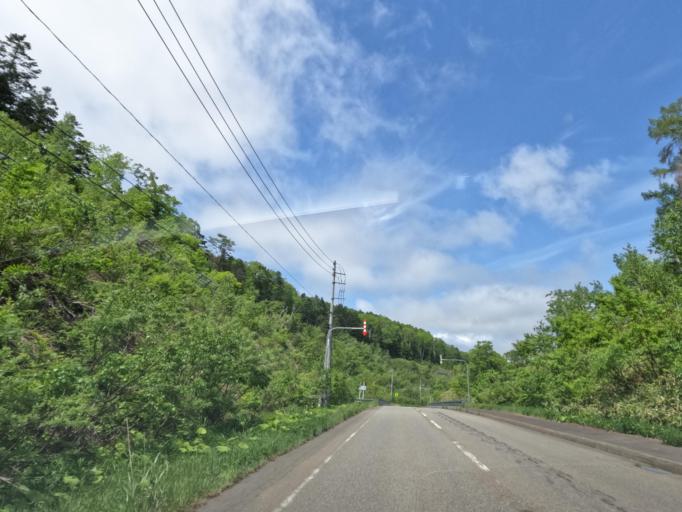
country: JP
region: Hokkaido
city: Tobetsu
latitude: 43.3245
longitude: 141.5707
